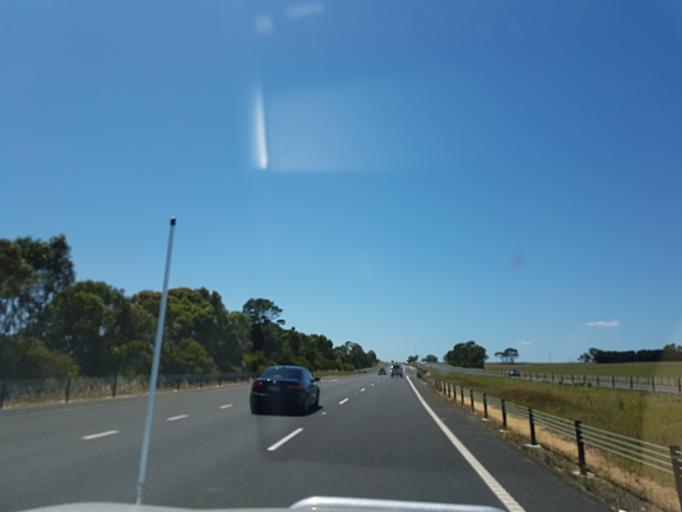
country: AU
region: Victoria
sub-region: Latrobe
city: Traralgon
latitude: -38.1578
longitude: 146.7170
